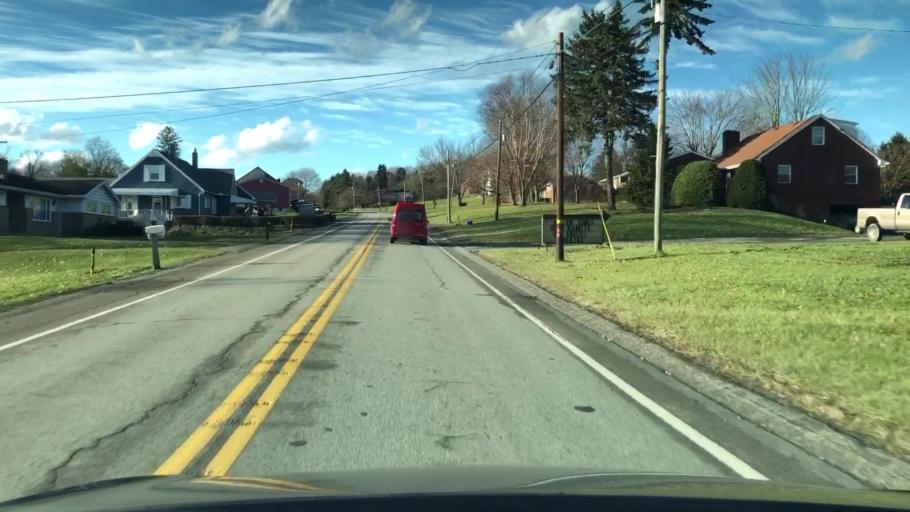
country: US
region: Pennsylvania
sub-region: Butler County
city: Meadowood
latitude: 40.8110
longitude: -79.8396
